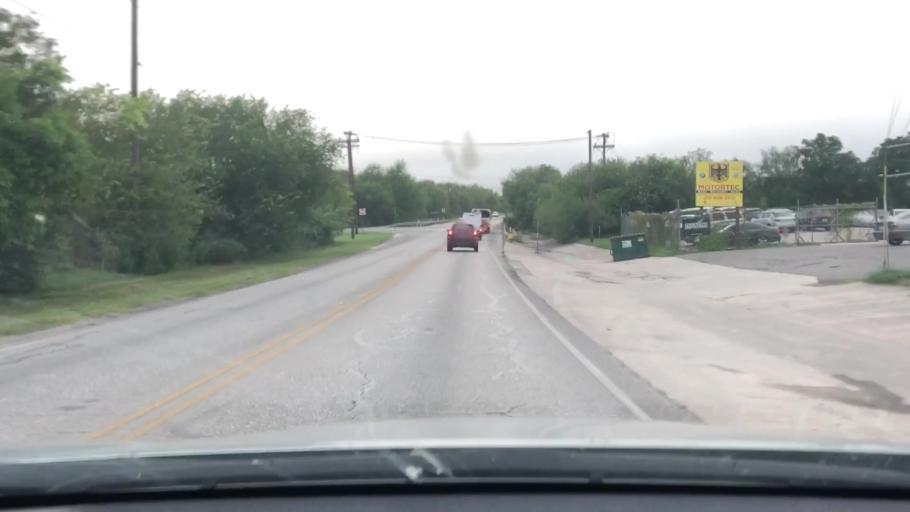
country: US
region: Texas
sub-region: Bexar County
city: Converse
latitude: 29.5155
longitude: -98.3215
